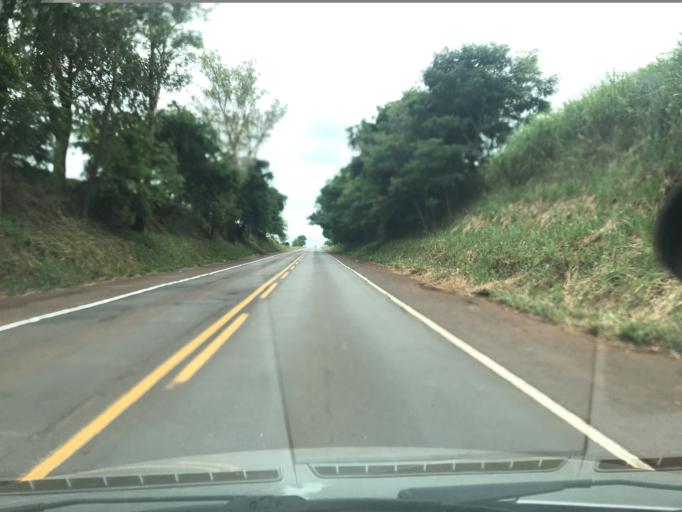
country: BR
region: Parana
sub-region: Terra Boa
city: Terra Boa
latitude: -23.5975
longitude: -52.3904
